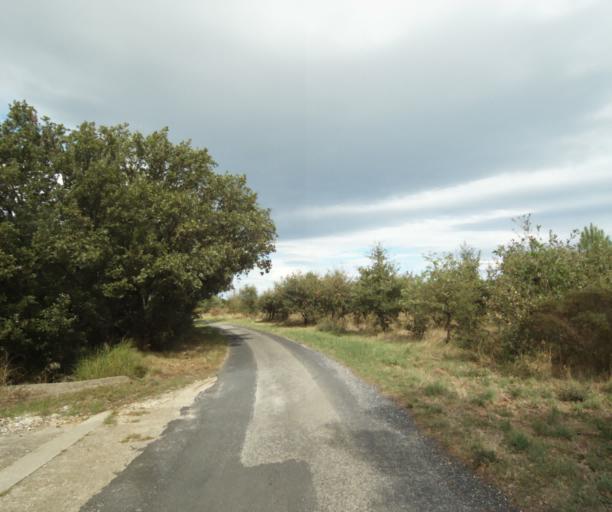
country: FR
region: Languedoc-Roussillon
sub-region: Departement des Pyrenees-Orientales
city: Argelers
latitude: 42.5370
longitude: 3.0173
